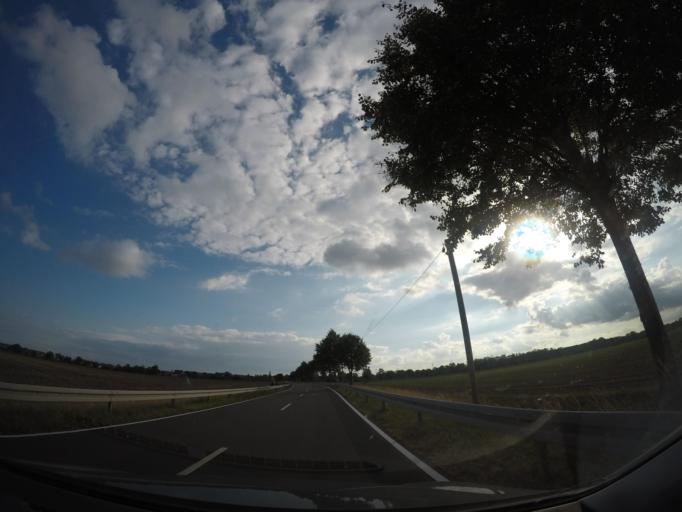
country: DE
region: Saxony-Anhalt
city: Mieste
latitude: 52.4136
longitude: 11.1235
